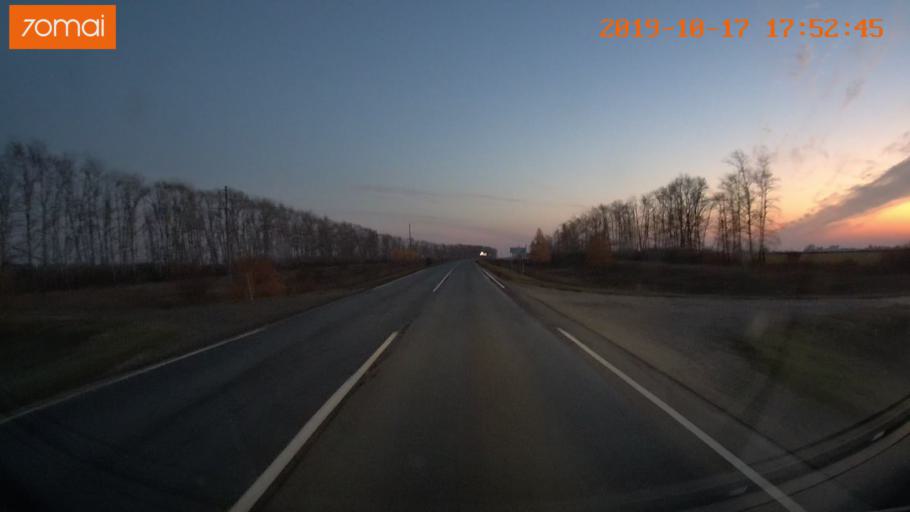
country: RU
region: Tula
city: Kurkino
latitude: 53.6301
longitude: 38.6820
